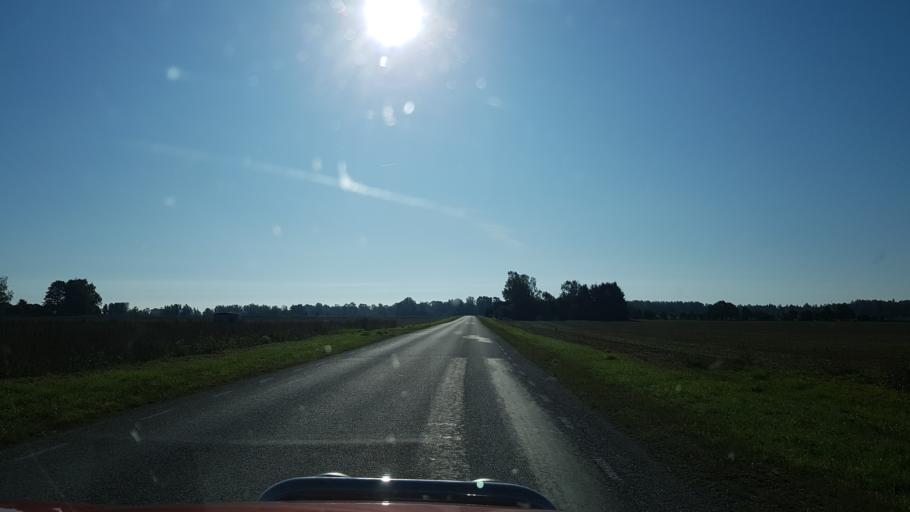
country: EE
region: Jogevamaa
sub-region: Tabivere vald
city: Tabivere
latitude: 58.6743
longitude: 26.6772
